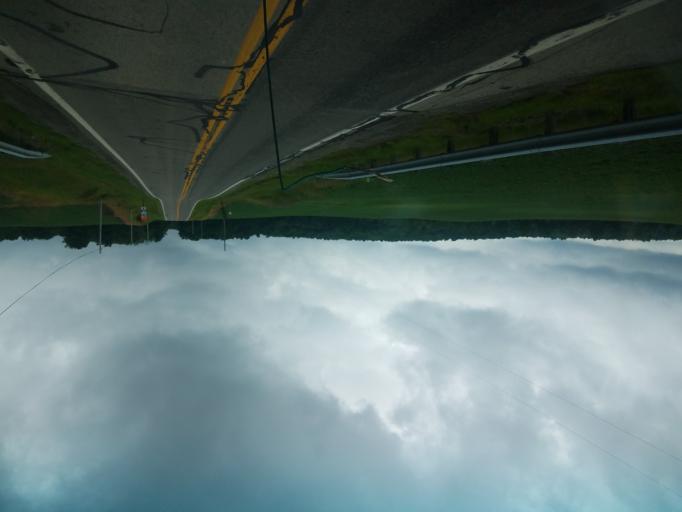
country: US
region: Ohio
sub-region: Logan County
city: Bellefontaine
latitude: 40.3837
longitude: -83.6170
